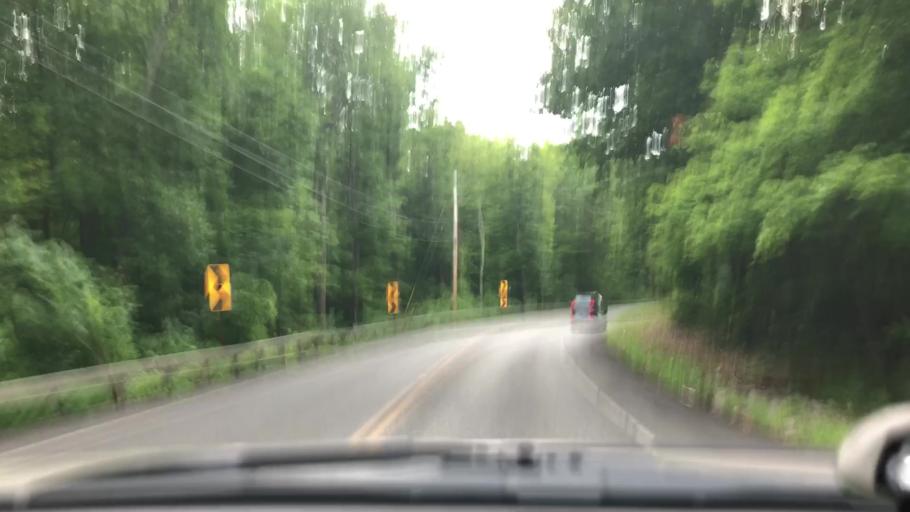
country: US
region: New York
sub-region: Saratoga County
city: Corinth
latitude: 43.1902
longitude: -73.7530
